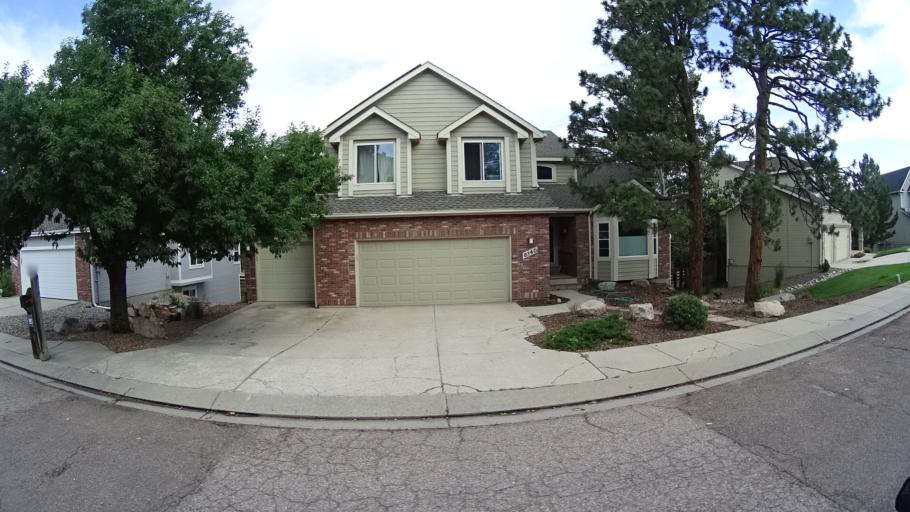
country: US
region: Colorado
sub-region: El Paso County
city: Air Force Academy
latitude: 38.9492
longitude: -104.8657
